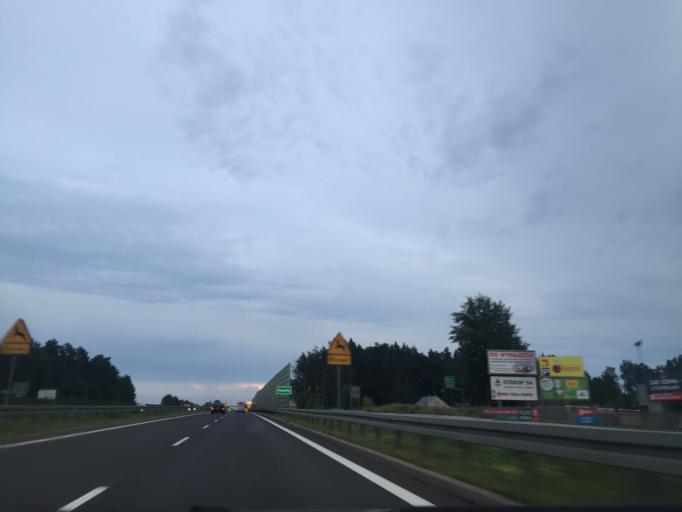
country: PL
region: Podlasie
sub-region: Powiat bialostocki
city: Choroszcz
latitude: 53.1511
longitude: 23.0445
